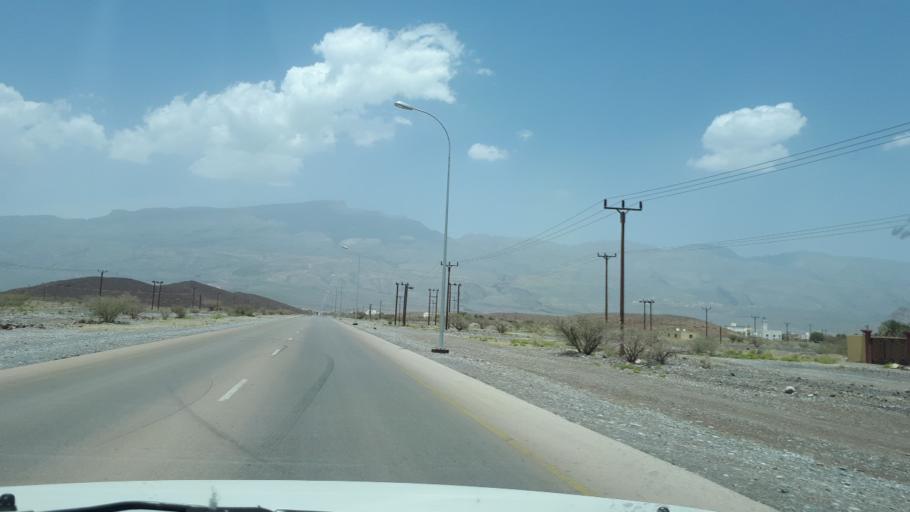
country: OM
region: Muhafazat ad Dakhiliyah
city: Bahla'
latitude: 23.0843
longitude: 57.2716
